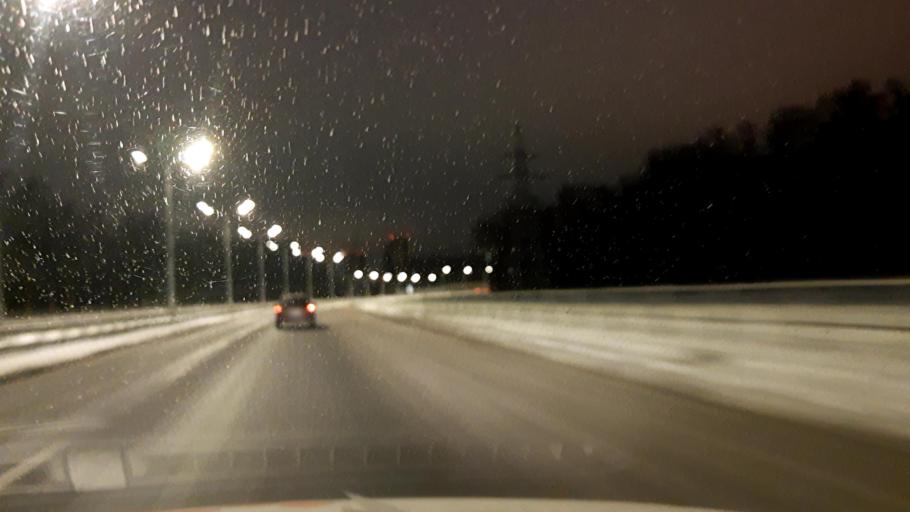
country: RU
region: Moskovskaya
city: Kommunarka
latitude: 55.5866
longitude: 37.4818
